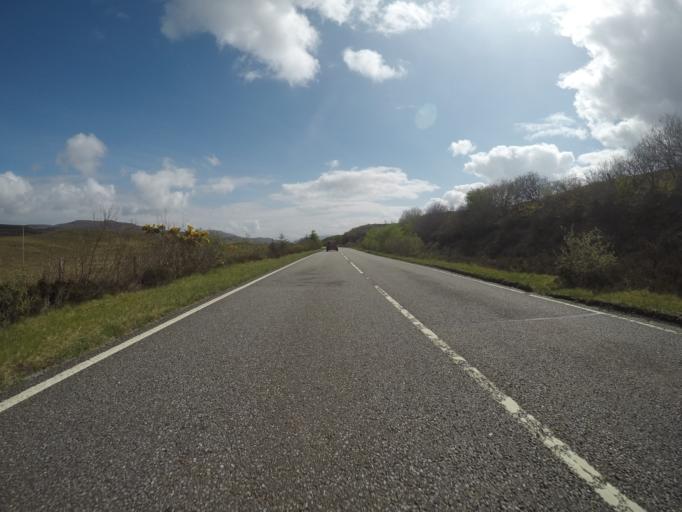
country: GB
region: Scotland
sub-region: Highland
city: Isle of Skye
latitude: 57.5072
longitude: -6.3360
